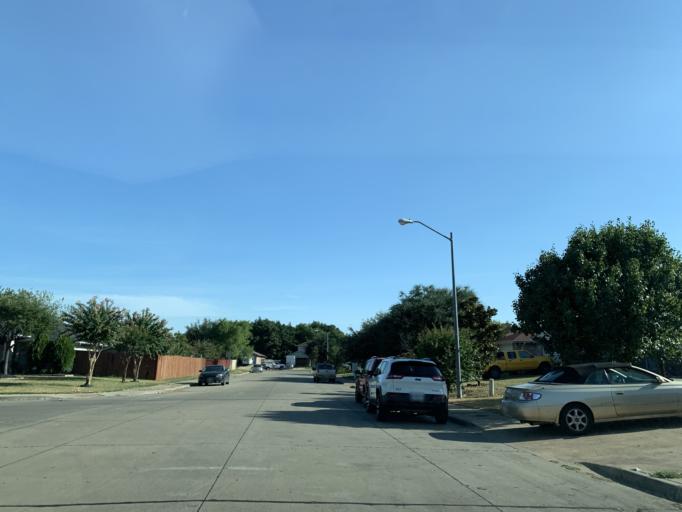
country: US
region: Texas
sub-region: Dallas County
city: Cockrell Hill
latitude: 32.7088
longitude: -96.8865
